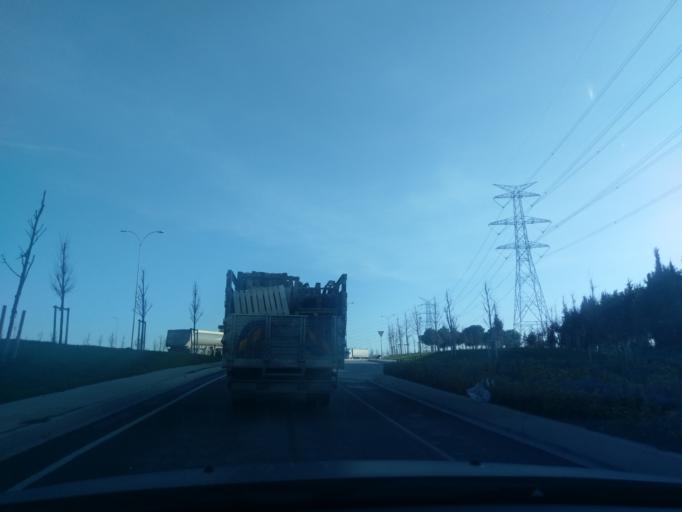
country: TR
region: Istanbul
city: Mahmutbey
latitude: 41.0701
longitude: 28.8275
